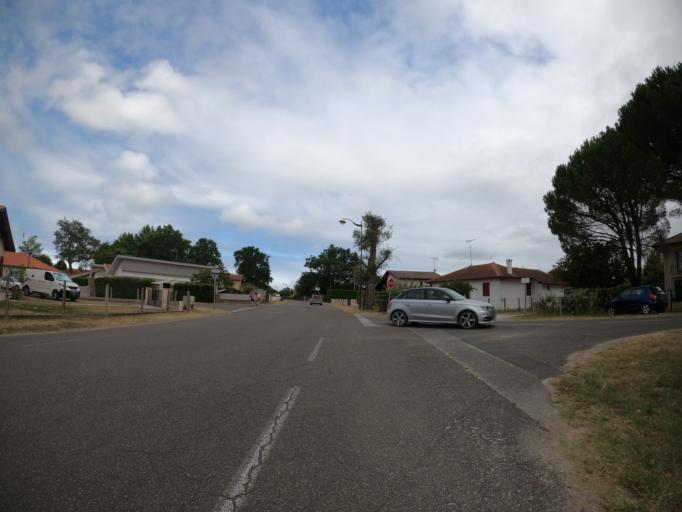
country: FR
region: Aquitaine
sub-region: Departement des Landes
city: Leon
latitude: 43.8809
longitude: -1.3054
